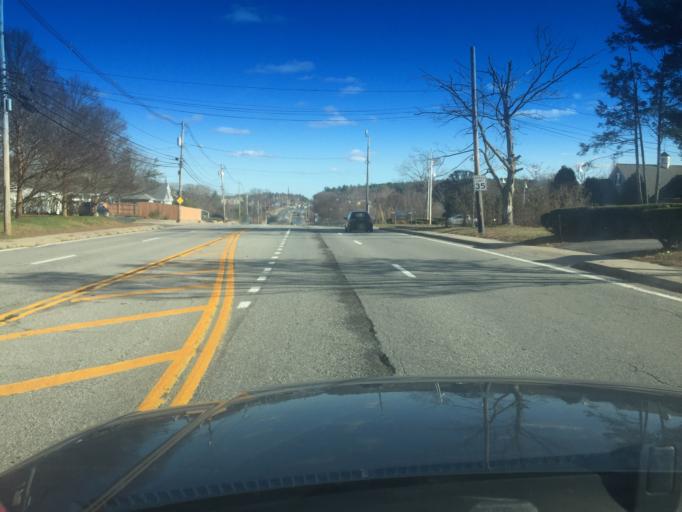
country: US
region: Rhode Island
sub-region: Providence County
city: Greenville
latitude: 41.8701
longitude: -71.5388
